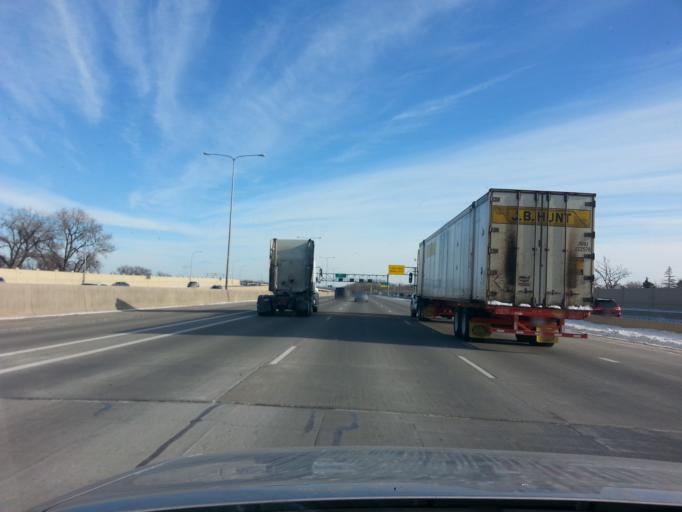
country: US
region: Minnesota
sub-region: Hennepin County
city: Richfield
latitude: 44.8900
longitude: -93.2831
